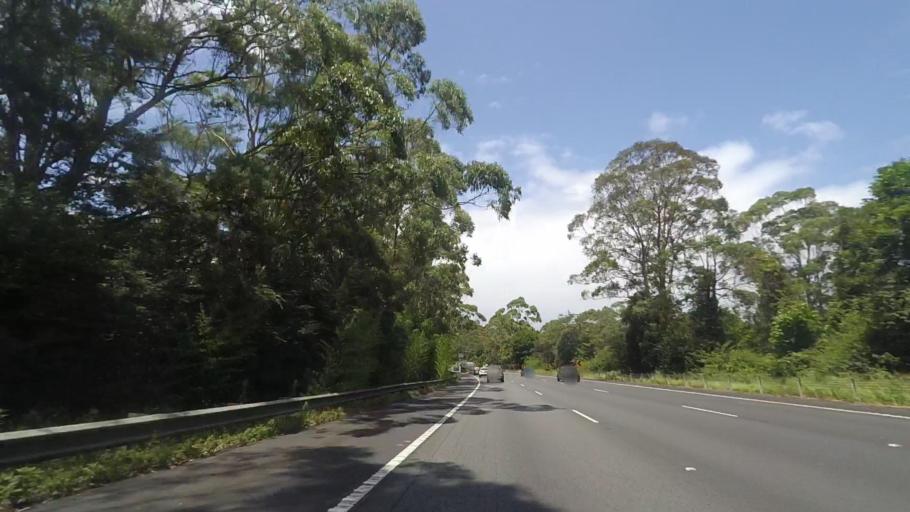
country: AU
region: New South Wales
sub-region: Gosford Shire
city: Lisarow
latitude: -33.3518
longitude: 151.3603
